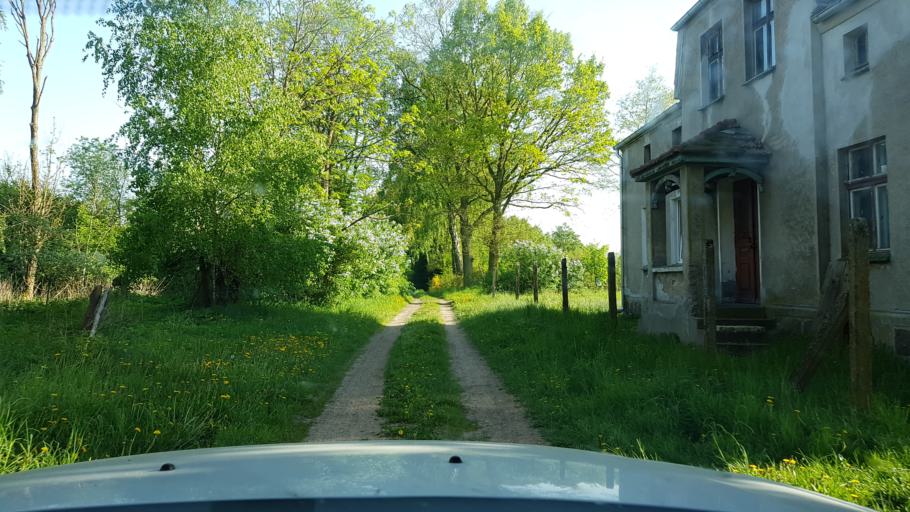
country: PL
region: West Pomeranian Voivodeship
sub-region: Powiat lobeski
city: Dobra
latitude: 53.6906
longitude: 15.3359
